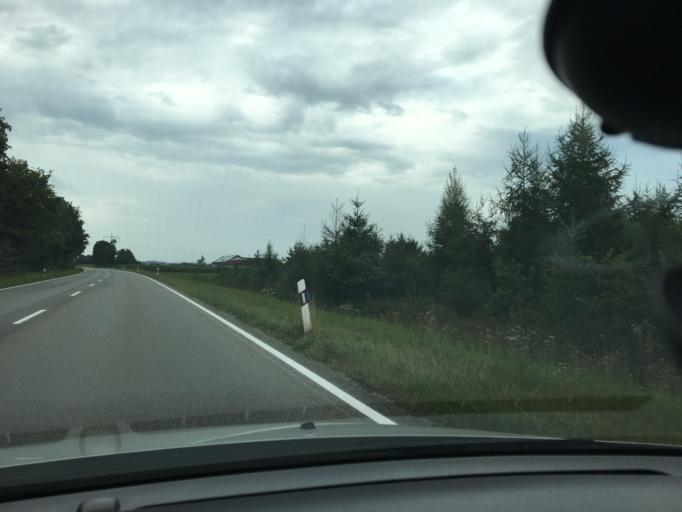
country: DE
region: Bavaria
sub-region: Upper Bavaria
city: Neufahrn
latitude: 48.2517
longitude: 12.4502
